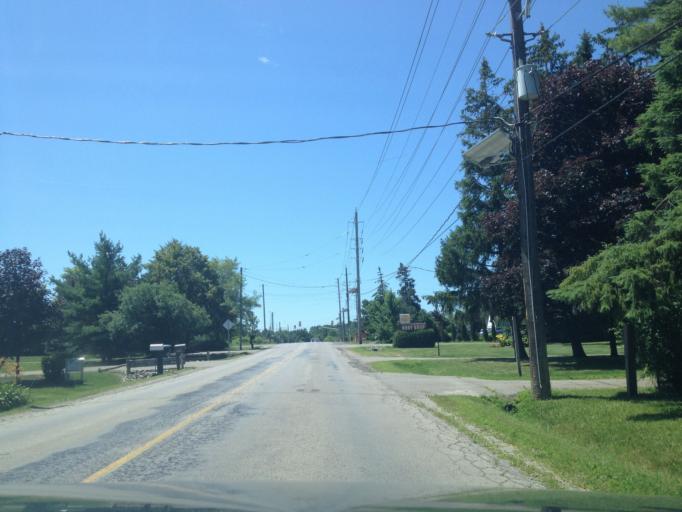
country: CA
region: Ontario
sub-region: Halton
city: Milton
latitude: 43.6576
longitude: -79.9572
